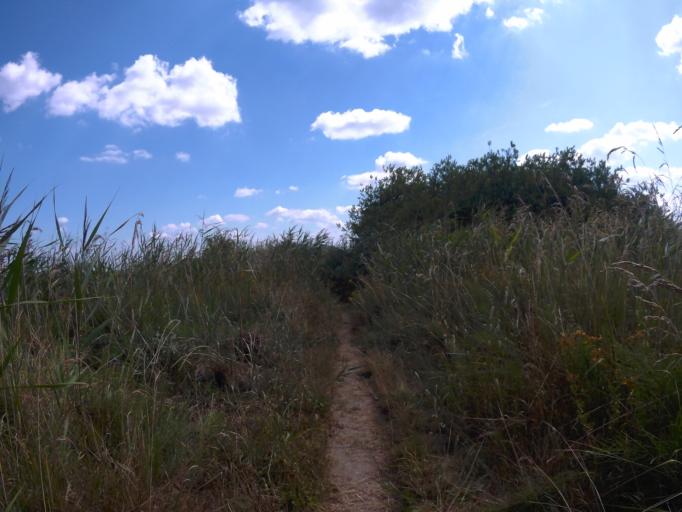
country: DE
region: Schleswig-Holstein
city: Hude
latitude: 54.3808
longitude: 9.2074
